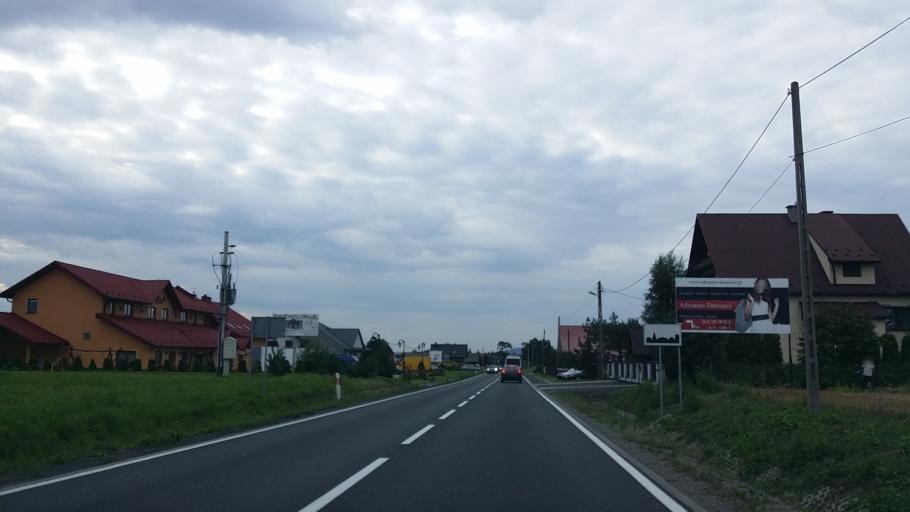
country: PL
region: Lesser Poland Voivodeship
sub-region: Powiat wadowicki
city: Spytkowice
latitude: 49.9932
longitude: 19.5173
